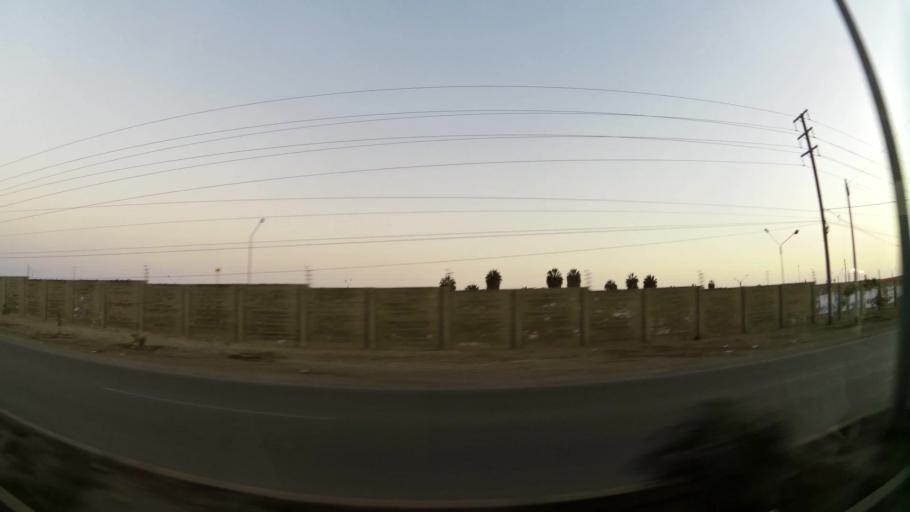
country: PE
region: Ica
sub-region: Provincia de Pisco
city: Pisco
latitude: -13.7110
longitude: -76.1926
